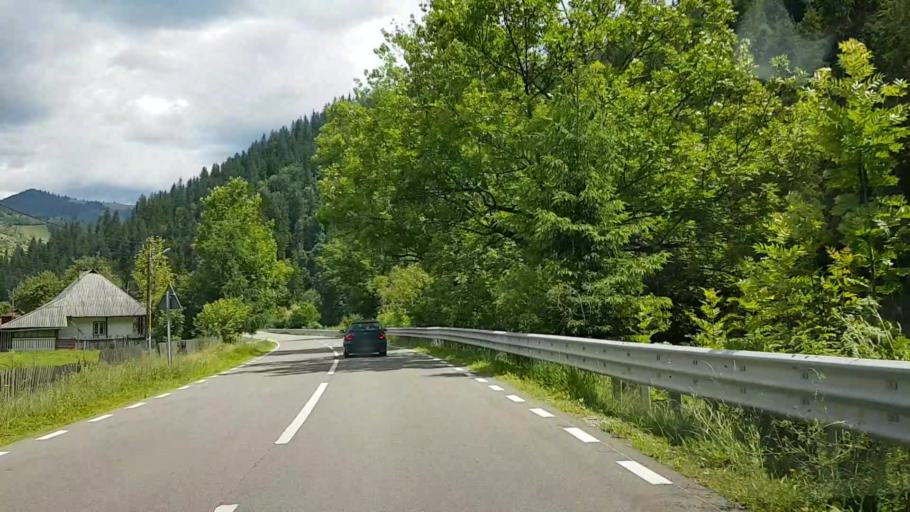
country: RO
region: Suceava
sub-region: Comuna Brosteni
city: Brosteni
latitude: 47.2560
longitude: 25.6717
